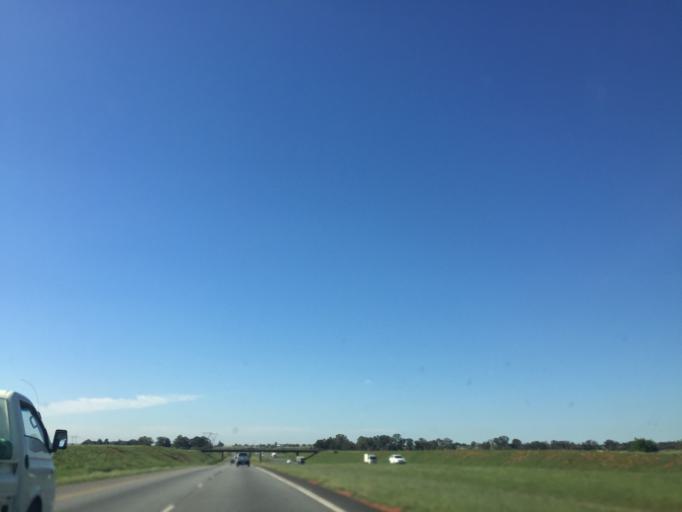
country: ZA
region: Gauteng
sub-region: Sedibeng District Municipality
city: Meyerton
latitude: -26.4483
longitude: 28.0726
